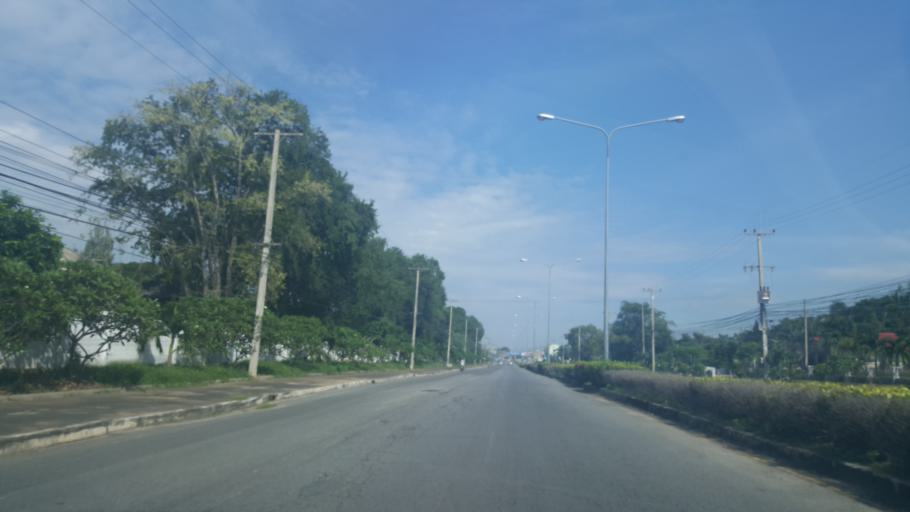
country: TH
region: Chon Buri
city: Sattahip
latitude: 12.6673
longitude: 100.8962
